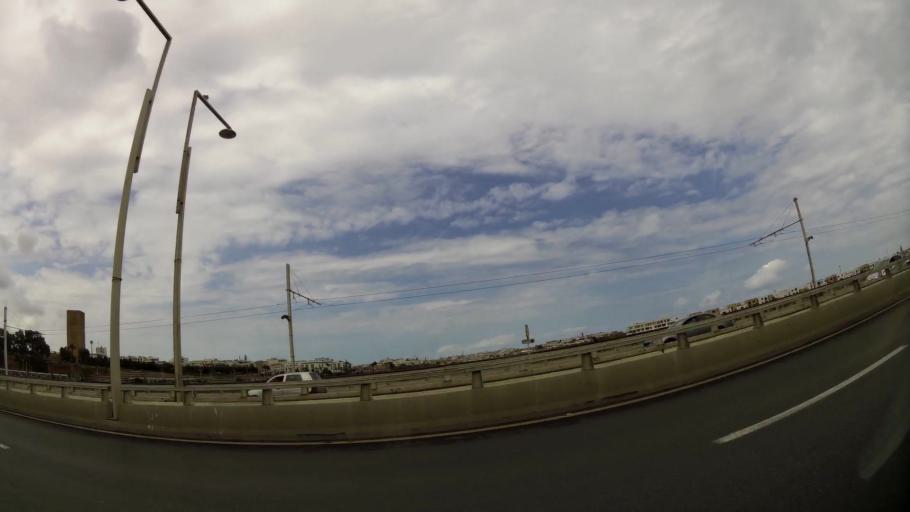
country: MA
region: Rabat-Sale-Zemmour-Zaer
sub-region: Rabat
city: Rabat
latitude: 34.0271
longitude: -6.8194
